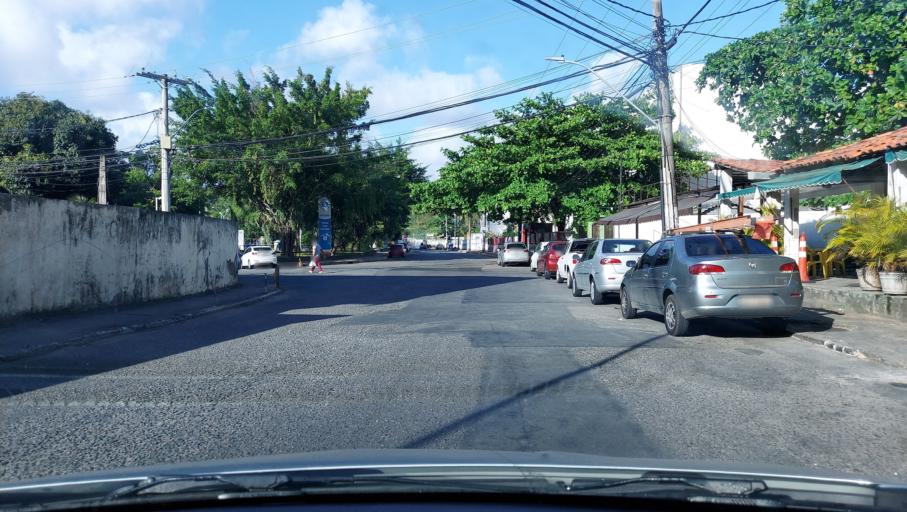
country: BR
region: Bahia
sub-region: Salvador
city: Salvador
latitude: -12.9803
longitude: -38.4483
